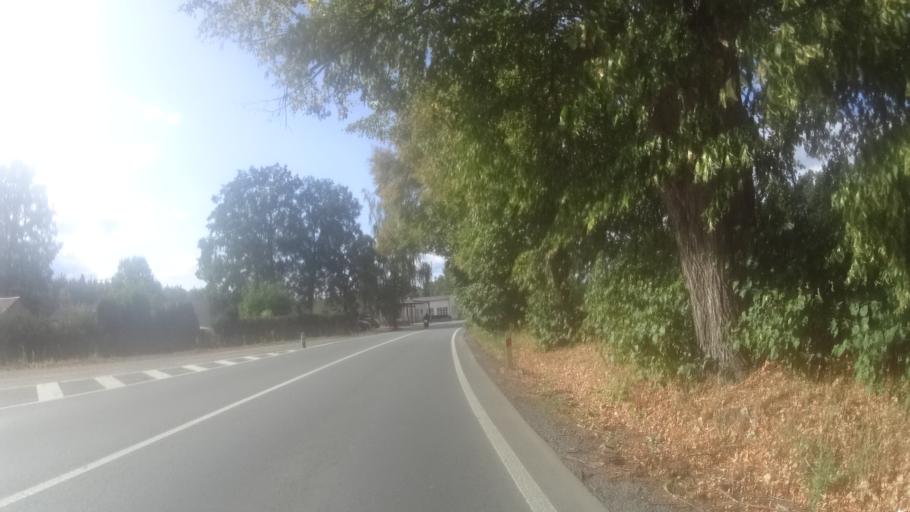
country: CZ
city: Borohradek
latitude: 50.1042
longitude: 16.0824
